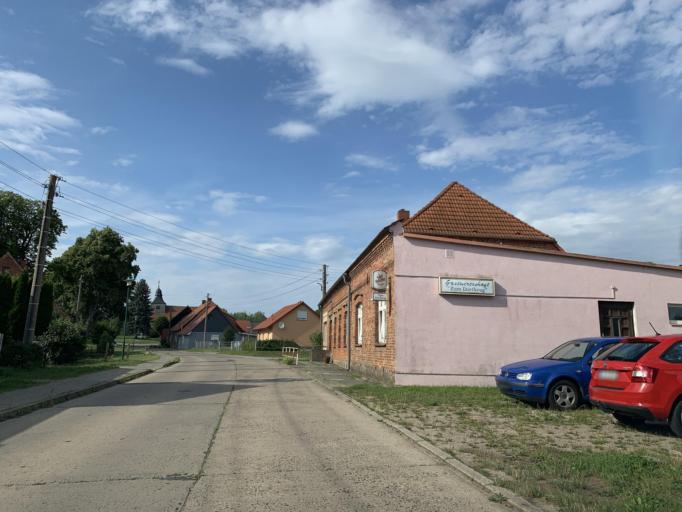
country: DE
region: Mecklenburg-Vorpommern
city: Carpin
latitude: 53.3761
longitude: 13.1814
